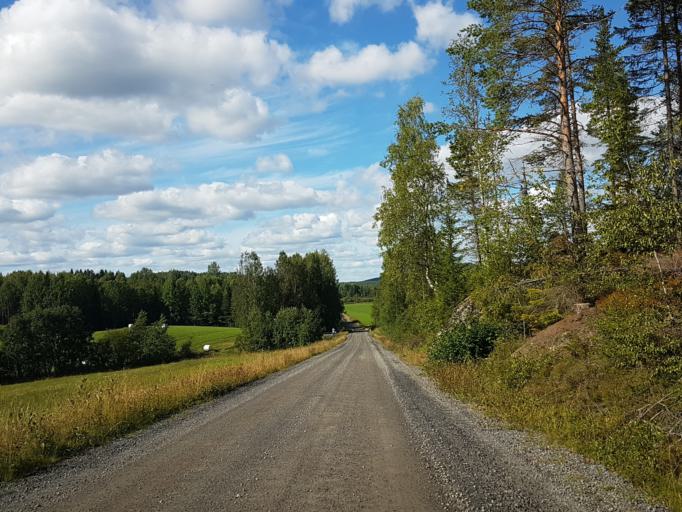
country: SE
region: Vaesterbotten
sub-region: Skelleftea Kommun
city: Burtraesk
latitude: 64.2872
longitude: 20.4585
